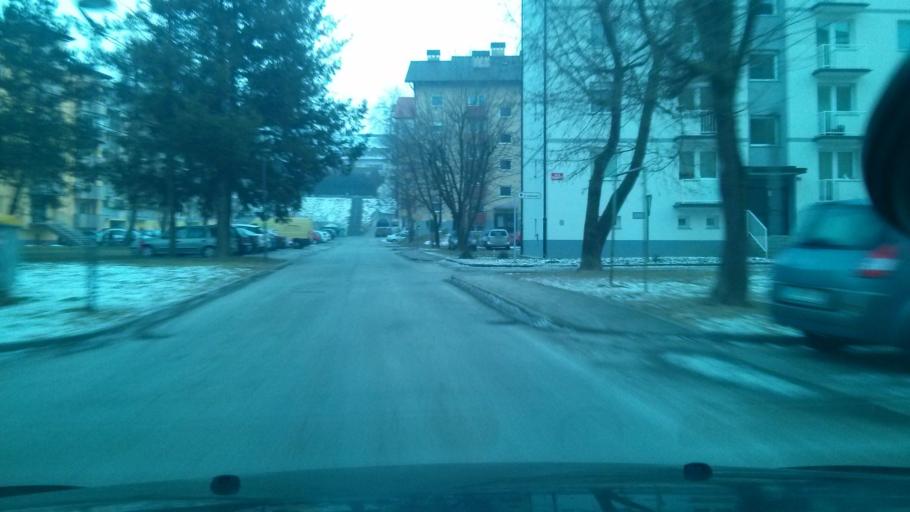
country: SI
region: Litija
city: Litija
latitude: 46.0578
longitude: 14.8368
